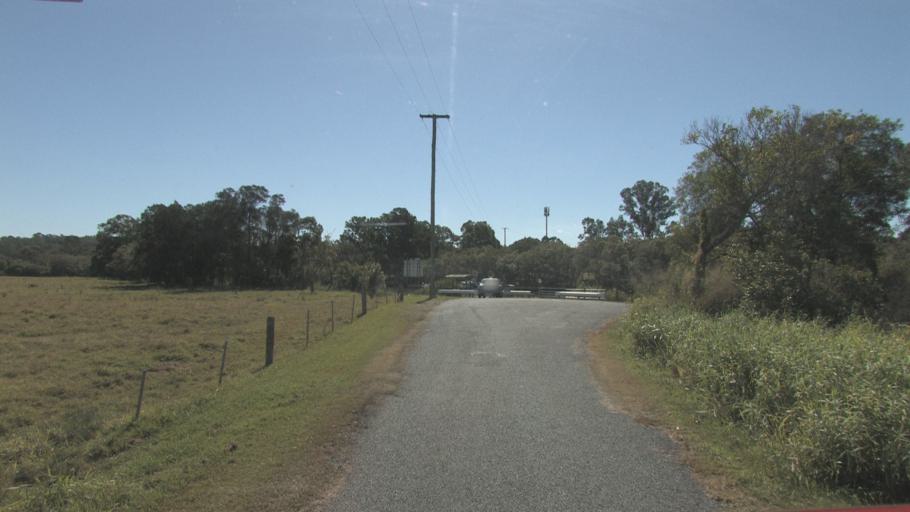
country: AU
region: Queensland
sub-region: Gold Coast
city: Yatala
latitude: -27.6810
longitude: 153.2259
